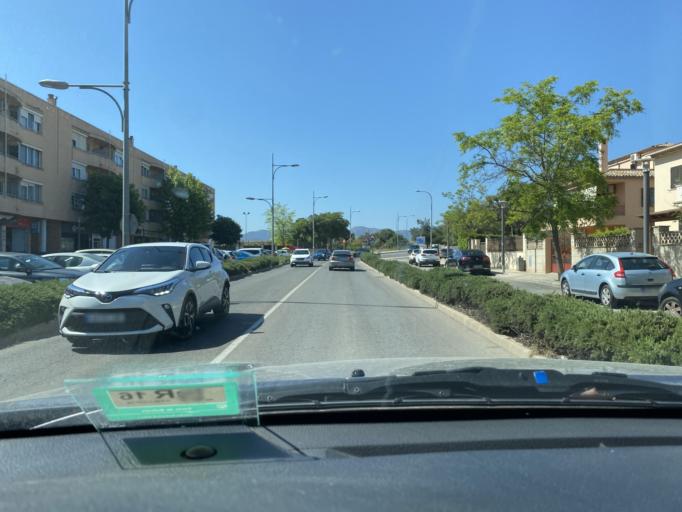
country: ES
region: Balearic Islands
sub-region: Illes Balears
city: Palma
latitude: 39.6041
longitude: 2.6868
